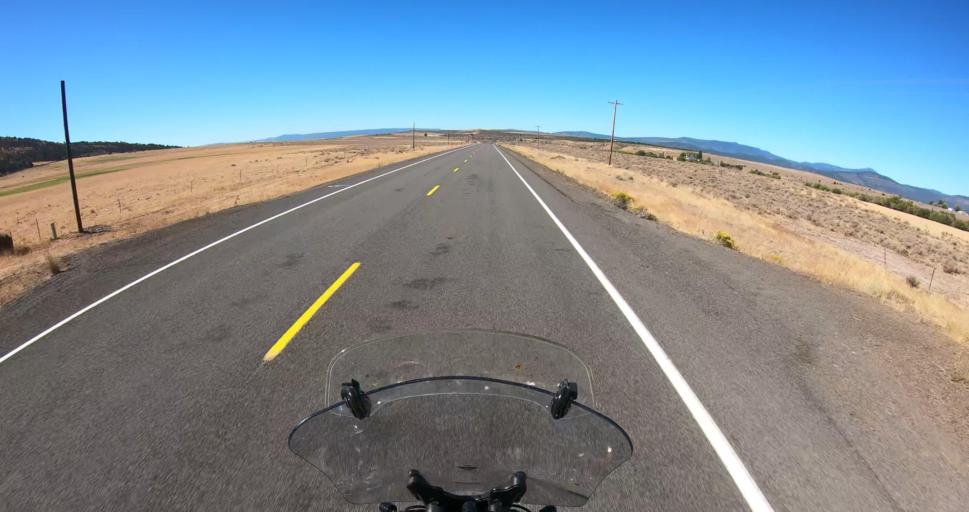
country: US
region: Oregon
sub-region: Lake County
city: Lakeview
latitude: 42.2610
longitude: -120.3496
